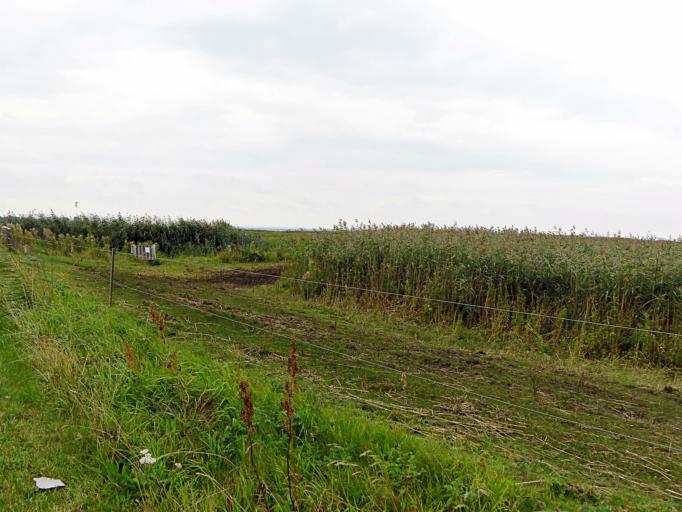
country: DK
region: Capital Region
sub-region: Fredensborg Kommune
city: Niva
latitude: 55.9297
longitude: 12.5198
